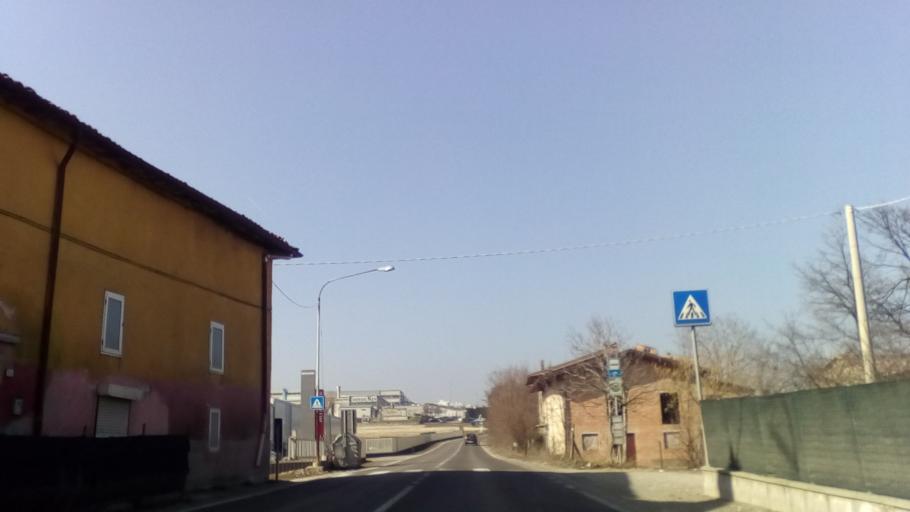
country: IT
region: Emilia-Romagna
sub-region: Provincia di Modena
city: Sant'Antonio
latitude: 44.3761
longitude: 10.8265
